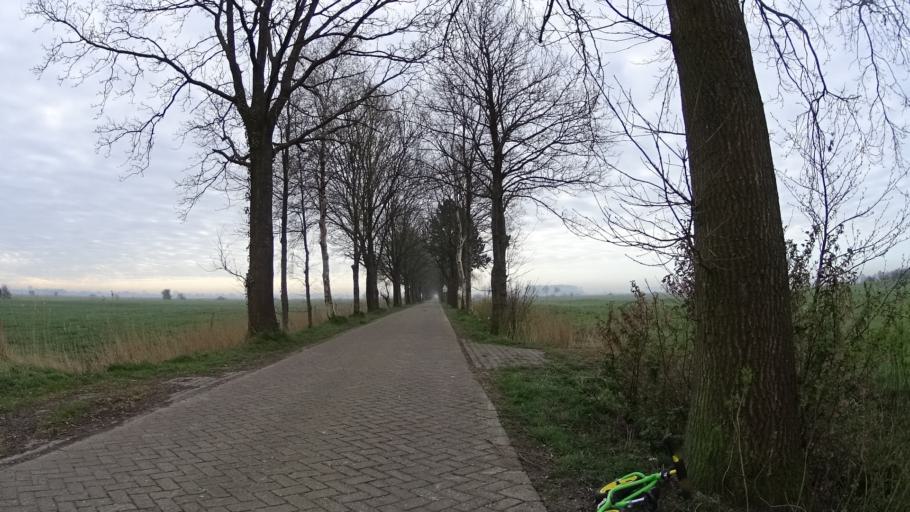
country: DE
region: Lower Saxony
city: Upgant-Schott
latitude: 53.4701
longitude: 7.3176
